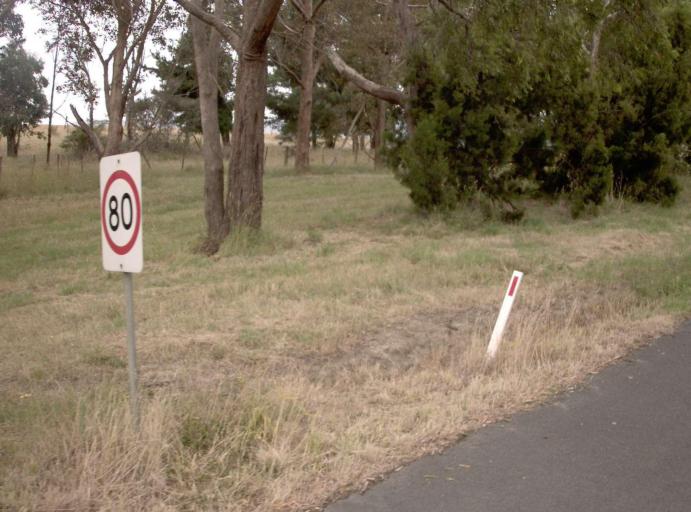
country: AU
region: Victoria
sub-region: Yarra Ranges
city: Healesville
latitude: -37.6759
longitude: 145.5067
